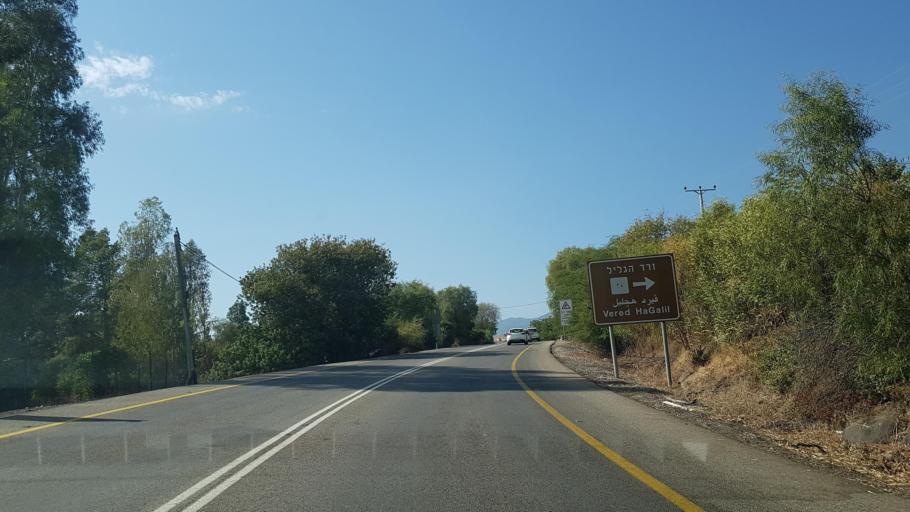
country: IL
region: Northern District
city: Rosh Pinna
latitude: 32.9035
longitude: 35.5519
